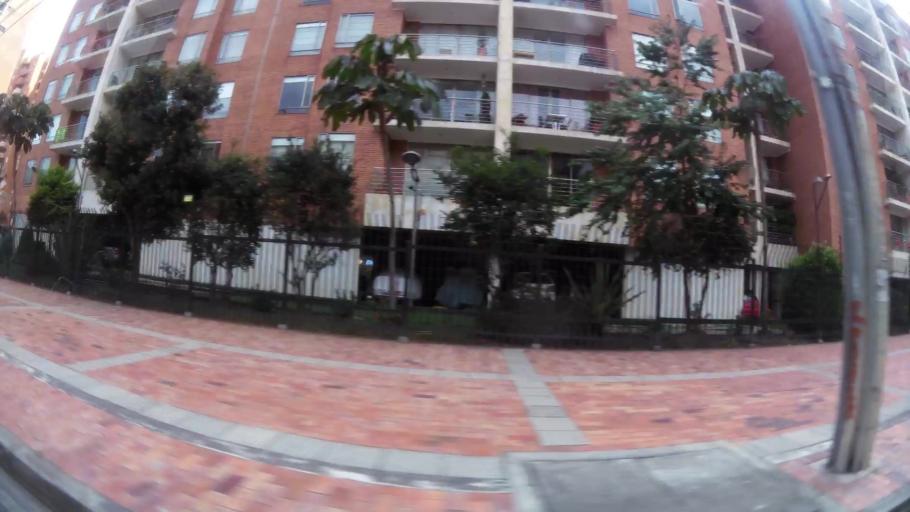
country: CO
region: Bogota D.C.
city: Barrio San Luis
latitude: 4.6864
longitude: -74.0379
